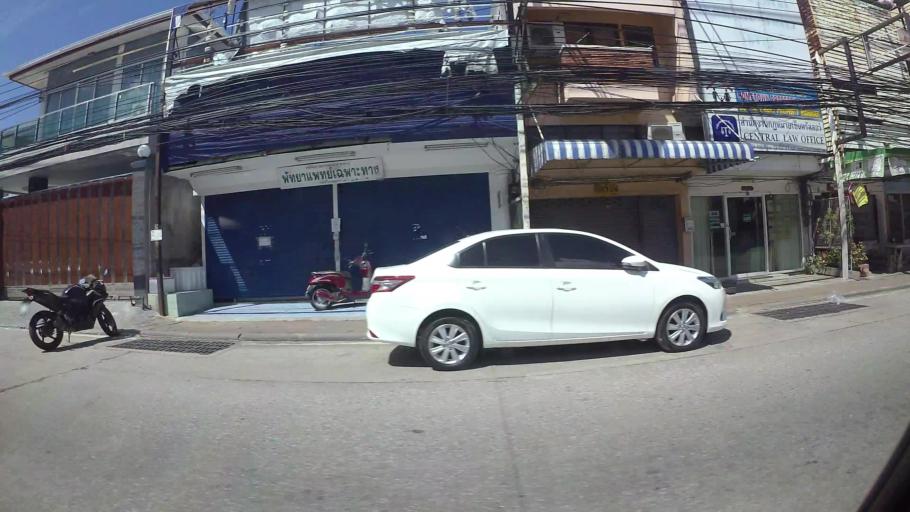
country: TH
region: Chon Buri
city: Phatthaya
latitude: 12.9343
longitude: 100.8930
